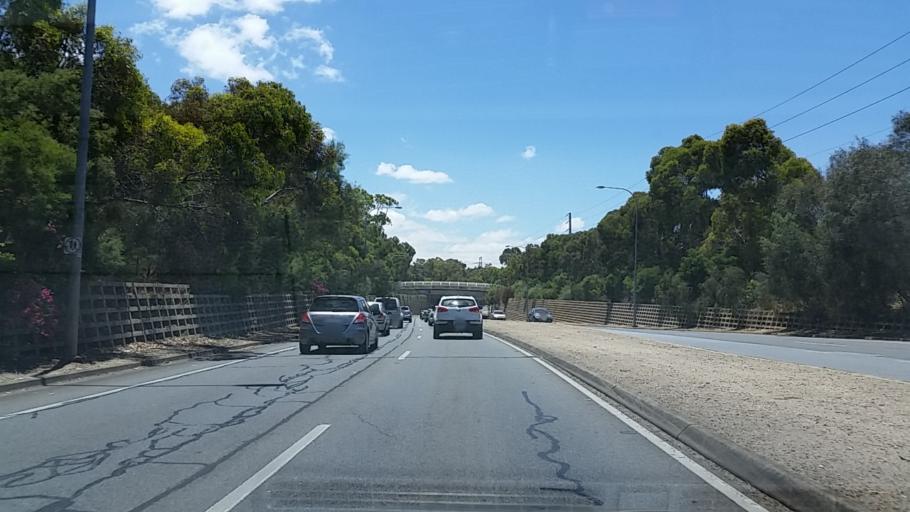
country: AU
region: South Australia
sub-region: Salisbury
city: Salisbury
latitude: -34.7624
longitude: 138.6411
